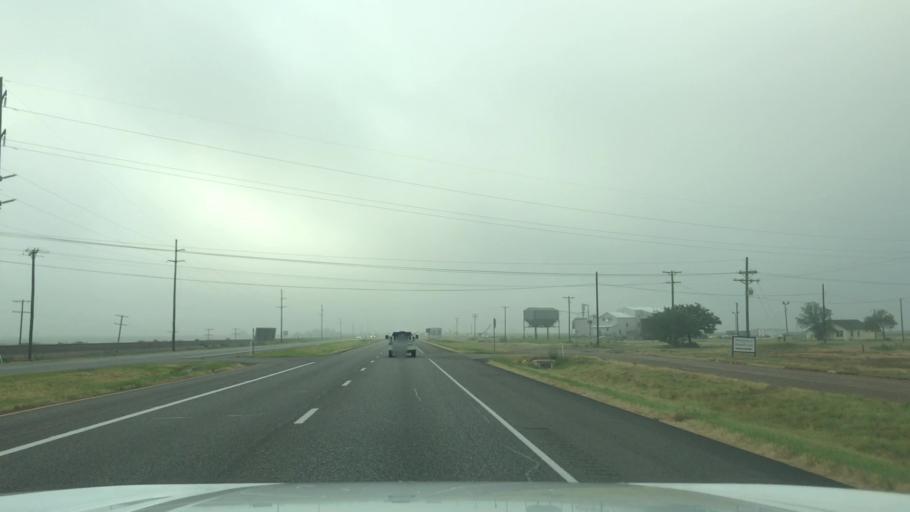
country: US
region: Texas
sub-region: Lubbock County
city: Ransom Canyon
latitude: 33.4827
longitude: -101.7110
